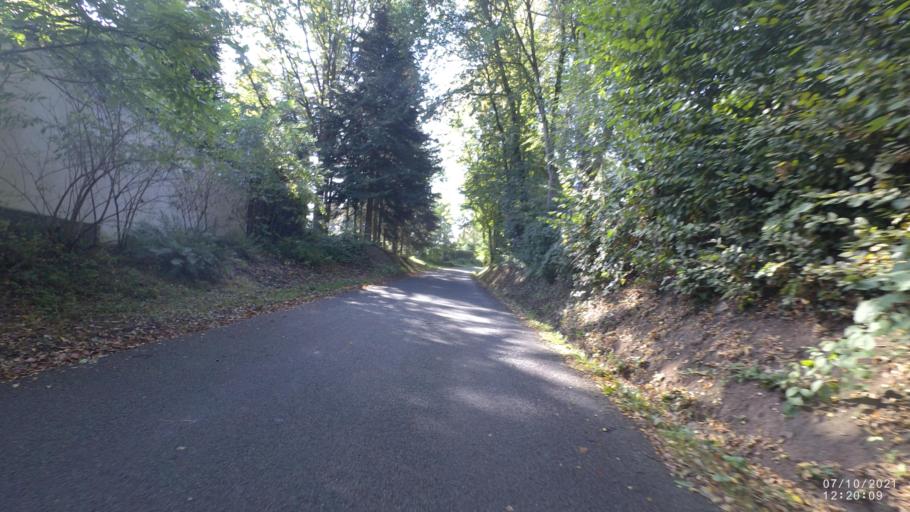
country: DE
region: North Rhine-Westphalia
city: Iserlohn
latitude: 51.4156
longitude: 7.7211
